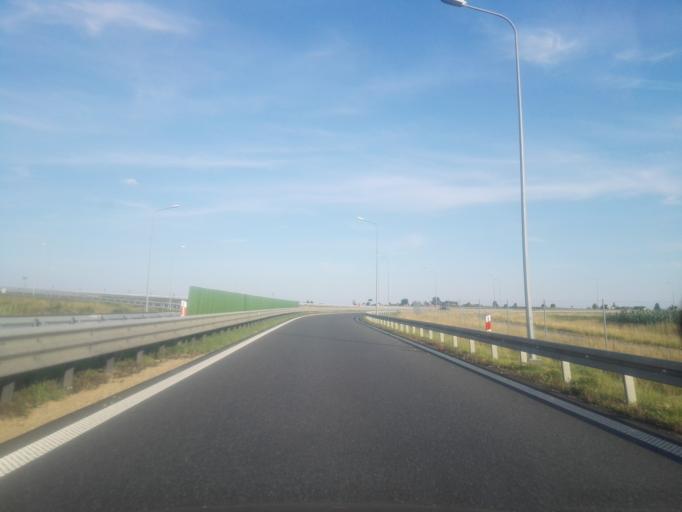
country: PL
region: Lodz Voivodeship
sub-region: Powiat wieruszowski
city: Walichnowy
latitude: 51.3152
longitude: 18.3838
